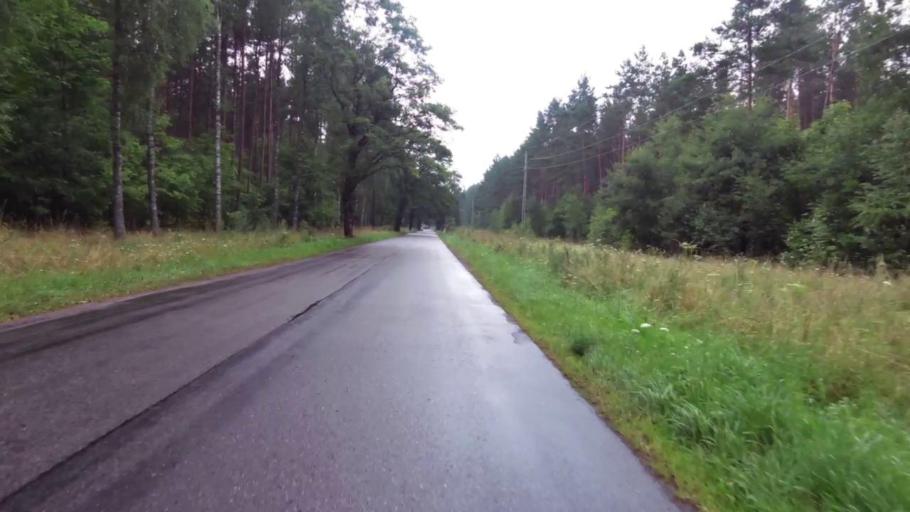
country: PL
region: West Pomeranian Voivodeship
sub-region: Powiat szczecinecki
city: Lubowo
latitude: 53.6013
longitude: 16.3658
